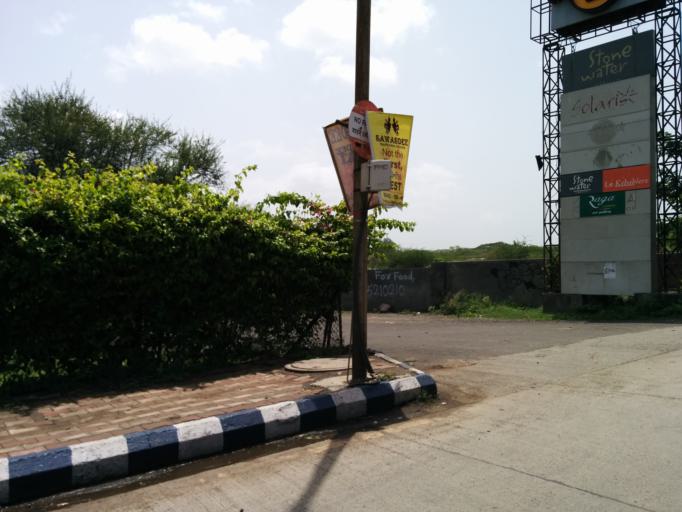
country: IN
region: Maharashtra
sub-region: Pune Division
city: Pune
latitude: 18.5352
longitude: 73.9121
